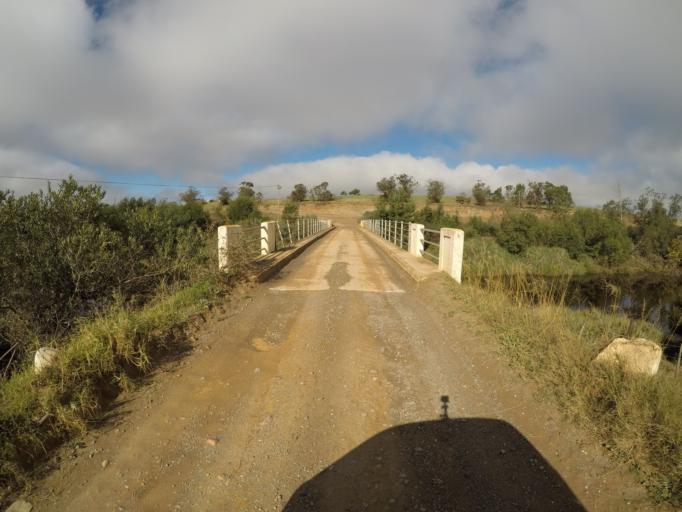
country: ZA
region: Western Cape
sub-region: Cape Winelands District Municipality
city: Ashton
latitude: -34.1278
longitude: 19.8401
